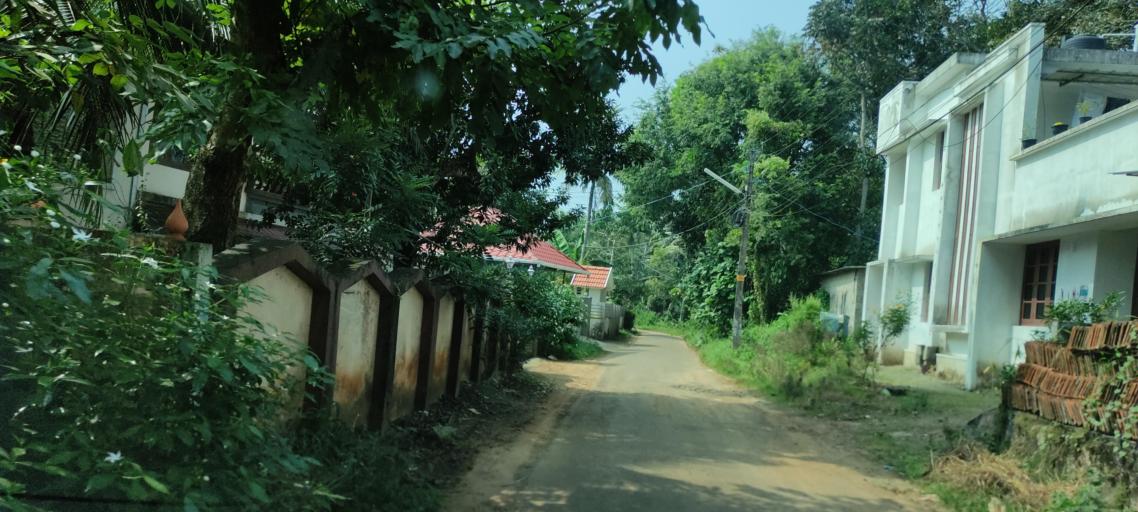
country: IN
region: Kerala
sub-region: Pattanamtitta
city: Adur
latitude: 9.2124
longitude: 76.6893
